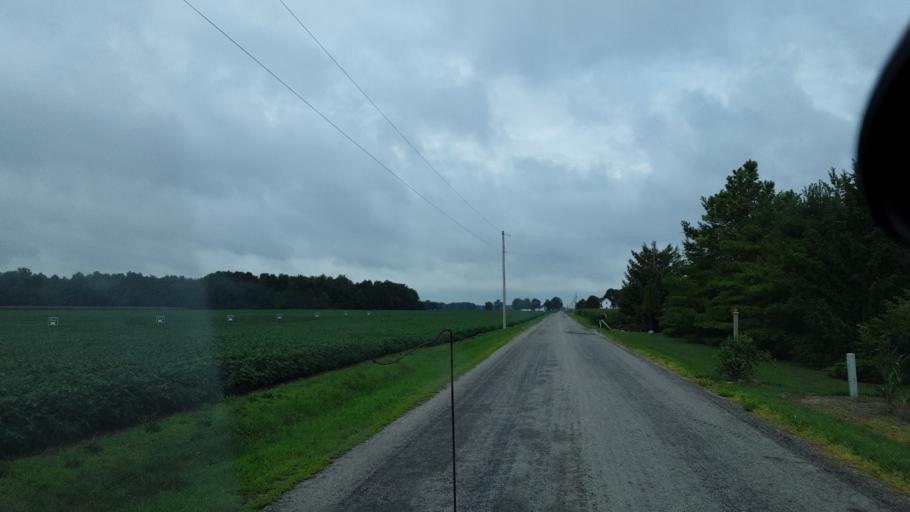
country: US
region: Indiana
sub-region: Allen County
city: Monroeville
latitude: 40.9215
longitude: -84.8447
